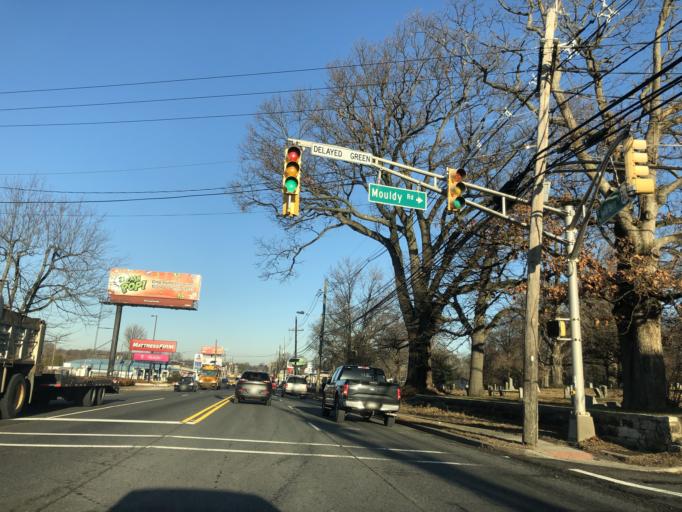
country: US
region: New Jersey
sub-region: Camden County
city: Barrington
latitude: 39.8700
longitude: -75.0427
